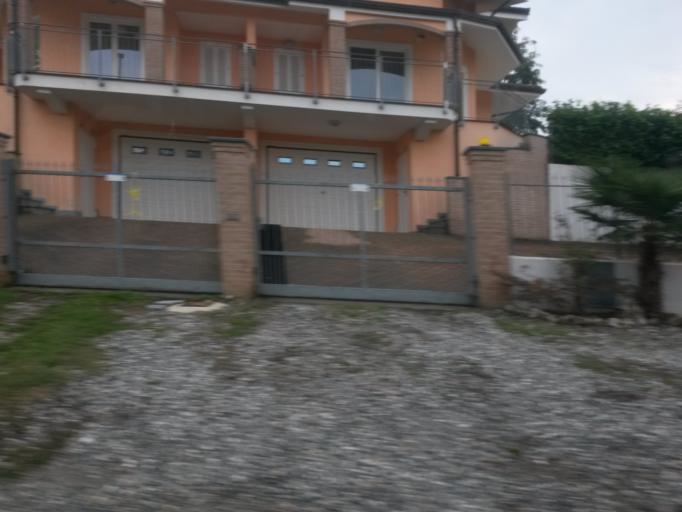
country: IT
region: Piedmont
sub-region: Provincia di Torino
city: Rosta
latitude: 45.0708
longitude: 7.4785
